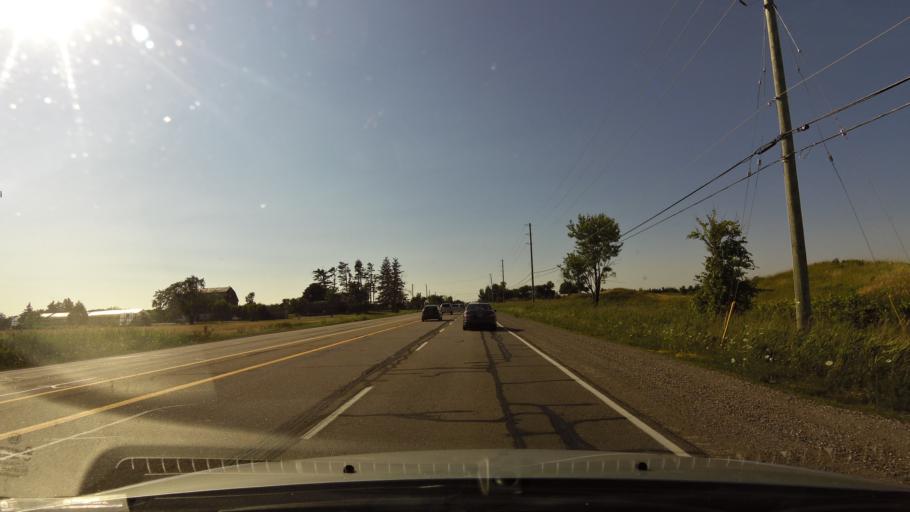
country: CA
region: Ontario
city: Oakville
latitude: 43.5246
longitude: -79.7663
